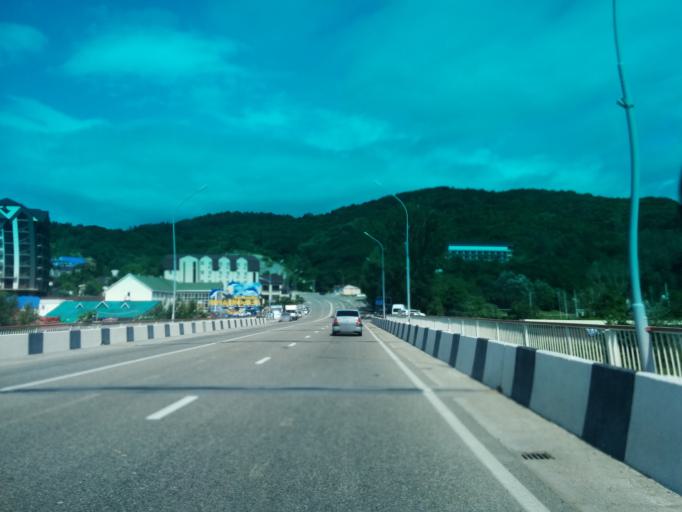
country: RU
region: Krasnodarskiy
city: Nebug
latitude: 44.1650
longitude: 39.0011
